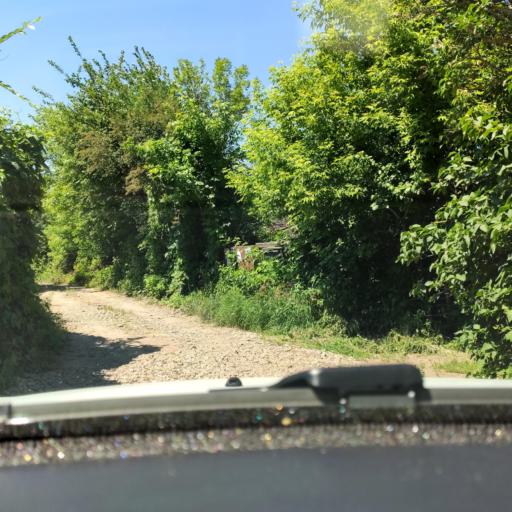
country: RU
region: Voronezj
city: Shilovo
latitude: 51.5941
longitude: 39.1436
